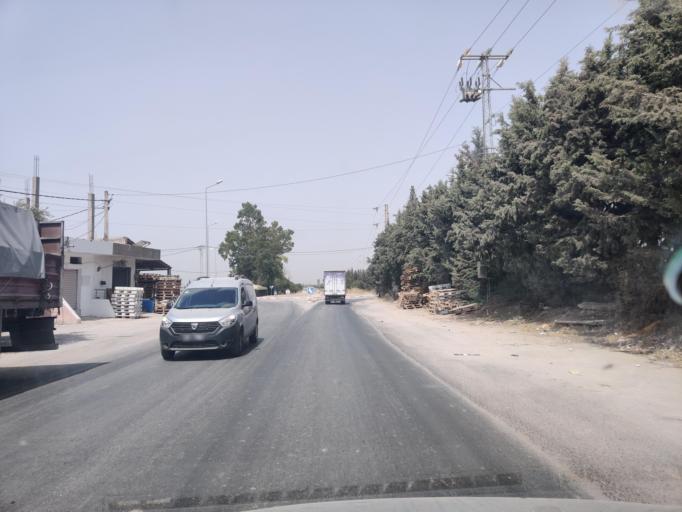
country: TN
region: Tunis
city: La Sebala du Mornag
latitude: 36.6625
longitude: 10.3230
